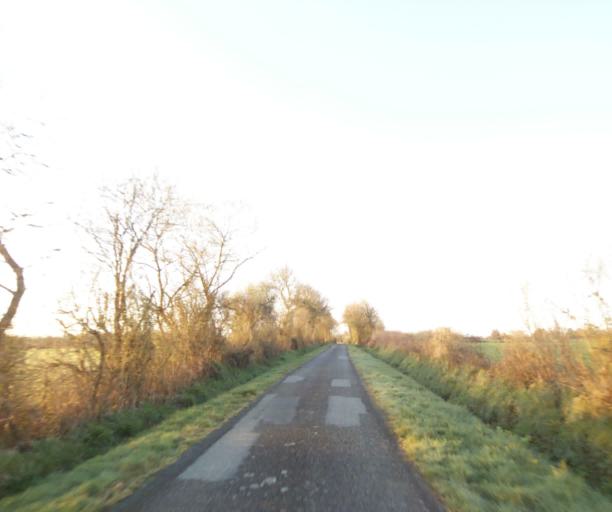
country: FR
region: Pays de la Loire
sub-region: Departement de la Loire-Atlantique
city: Bouvron
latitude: 47.4281
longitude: -1.8835
